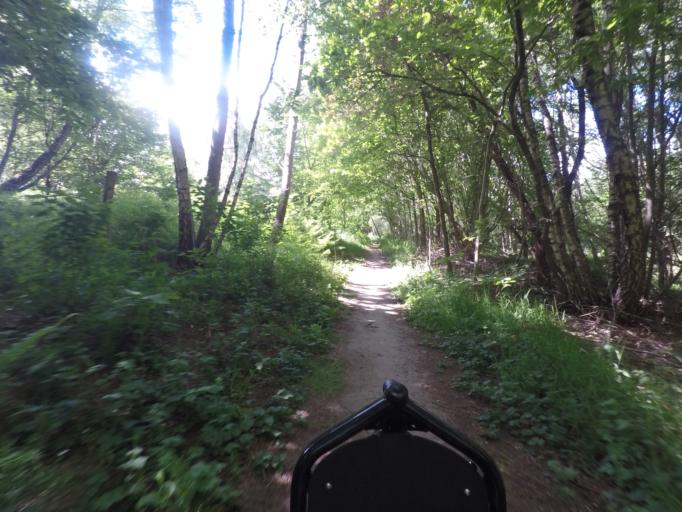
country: DE
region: Schleswig-Holstein
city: Stapelfeld
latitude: 53.6255
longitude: 10.2215
